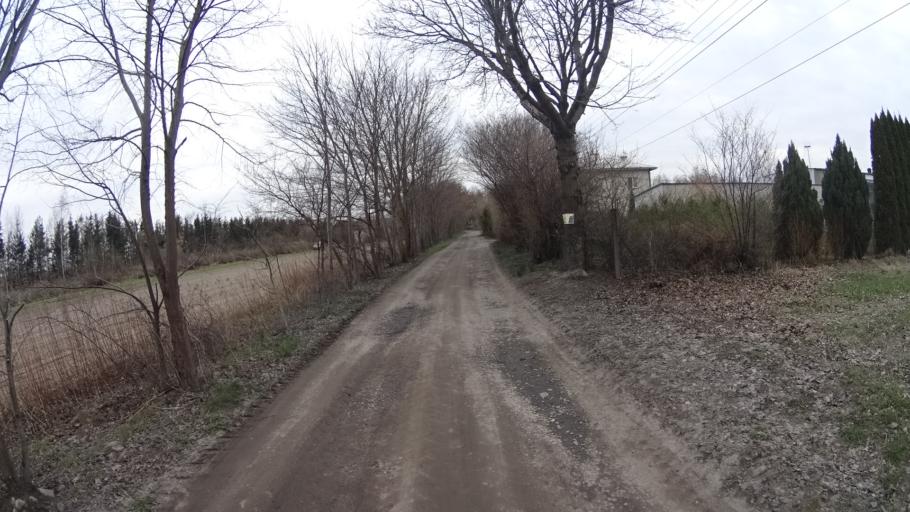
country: PL
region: Masovian Voivodeship
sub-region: Powiat warszawski zachodni
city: Jozefow
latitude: 52.2464
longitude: 20.6778
